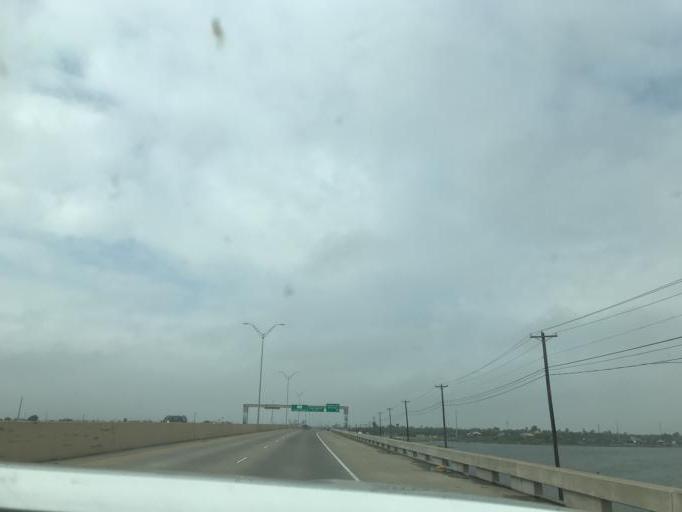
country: US
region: Texas
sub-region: Nueces County
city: Corpus Christi
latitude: 27.6625
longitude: -97.2702
